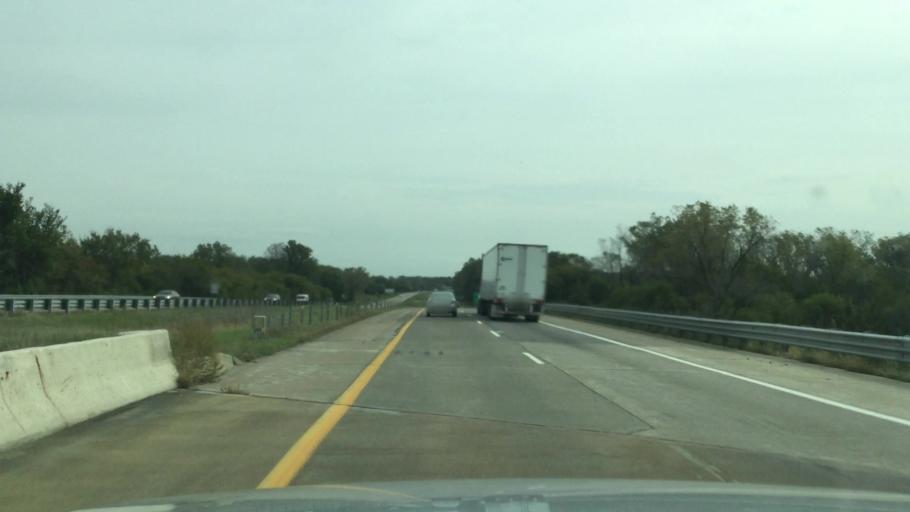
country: US
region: Michigan
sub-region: Shiawassee County
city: Durand
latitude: 42.9627
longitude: -83.9500
